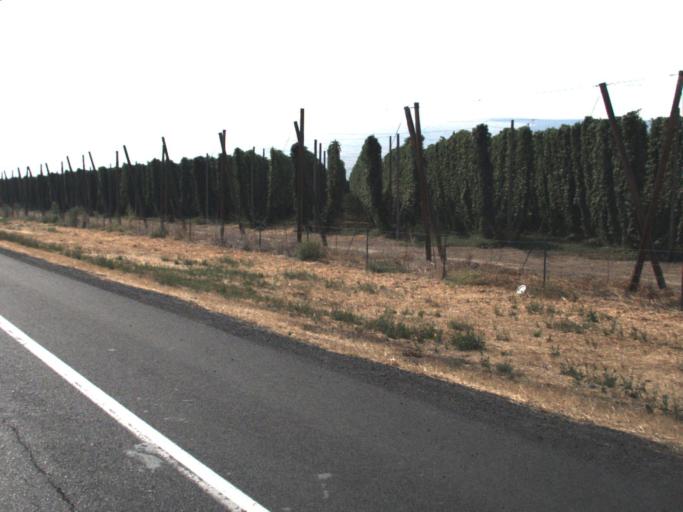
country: US
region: Washington
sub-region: Yakima County
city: Terrace Heights
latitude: 46.5562
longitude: -120.3932
